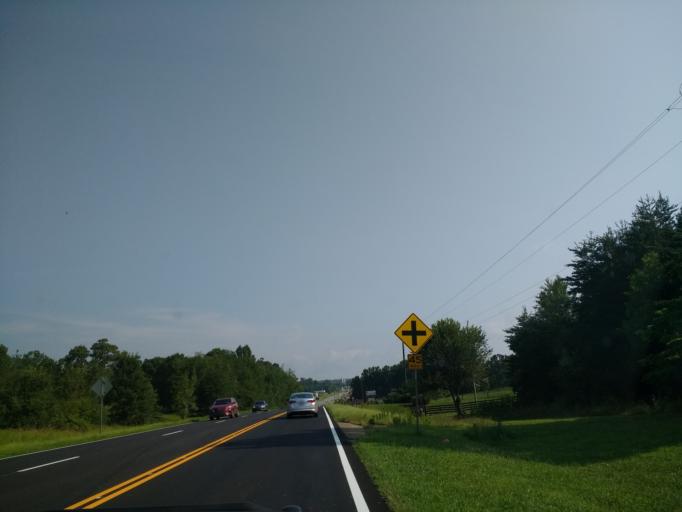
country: US
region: Georgia
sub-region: White County
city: Cleveland
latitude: 34.4997
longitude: -83.7562
